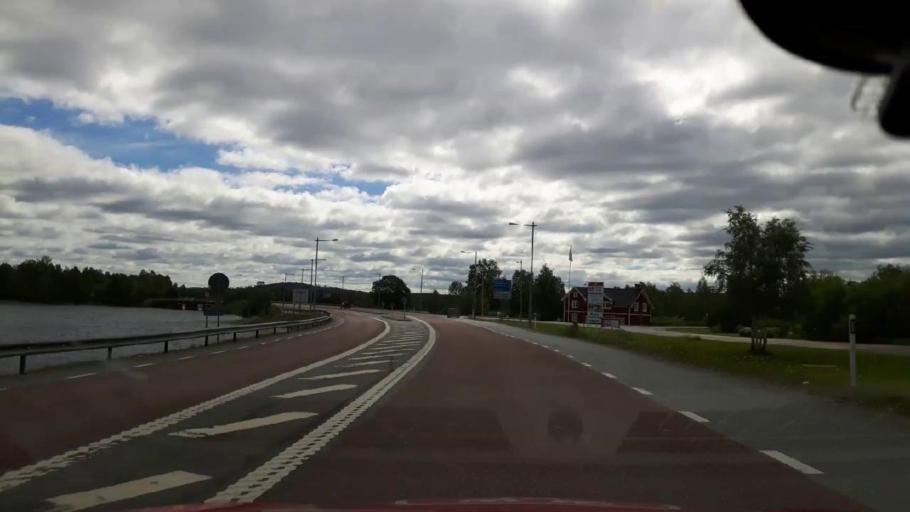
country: SE
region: Jaemtland
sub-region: Braecke Kommun
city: Braecke
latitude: 62.9188
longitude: 15.2380
